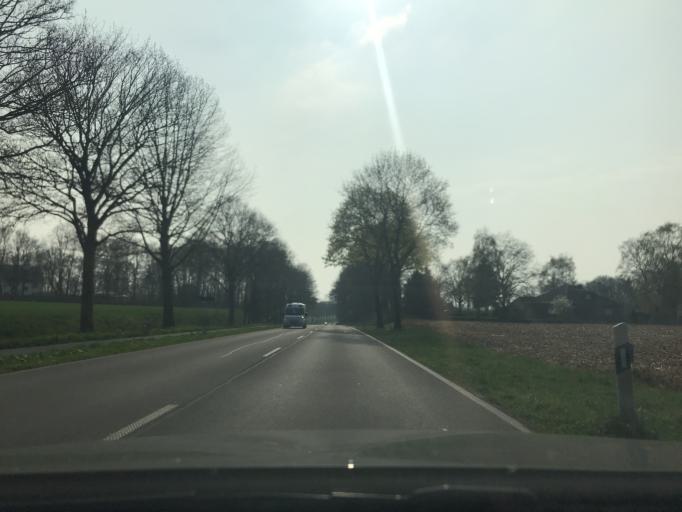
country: DE
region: North Rhine-Westphalia
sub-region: Regierungsbezirk Dusseldorf
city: Goch
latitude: 51.6875
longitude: 6.1903
